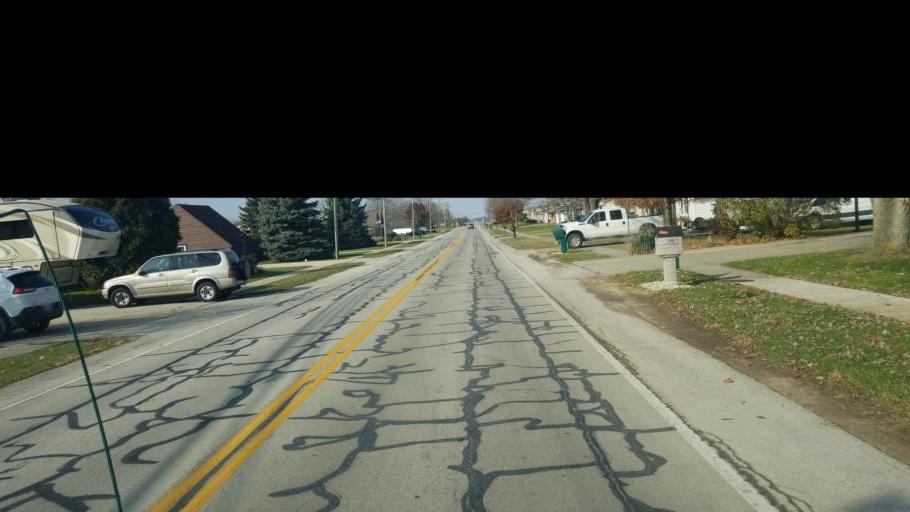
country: US
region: Ohio
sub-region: Mercer County
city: Celina
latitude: 40.5620
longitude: -84.5831
